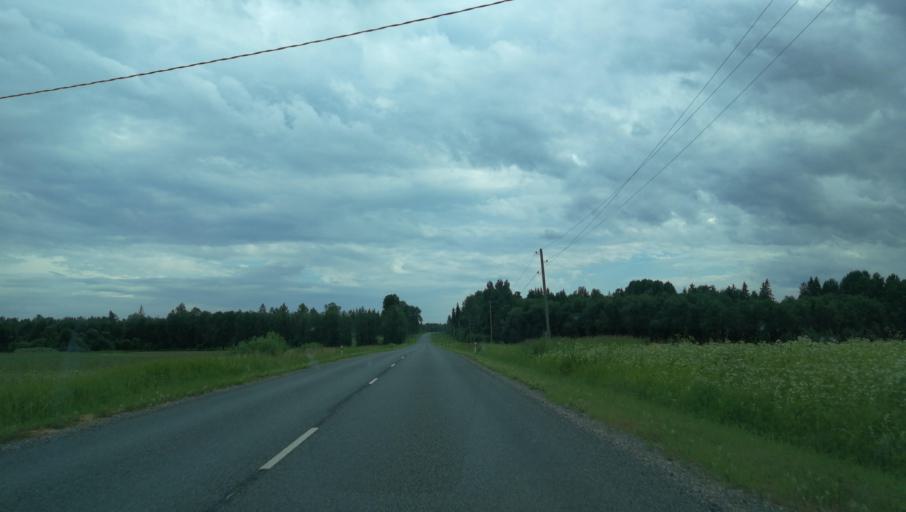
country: LV
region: Naukseni
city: Naukseni
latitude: 57.7553
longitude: 25.4324
